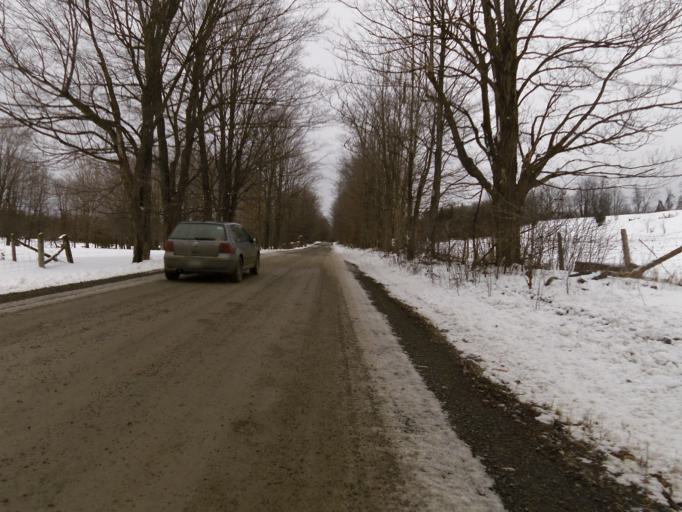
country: CA
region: Ontario
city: Carleton Place
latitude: 45.1350
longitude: -76.2496
